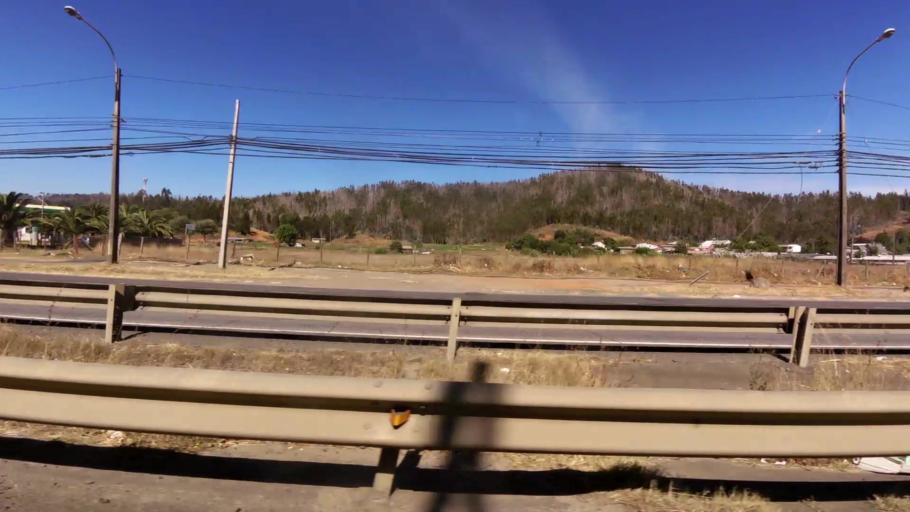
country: CL
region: Biobio
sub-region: Provincia de Concepcion
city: Concepcion
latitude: -36.7902
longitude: -73.0245
